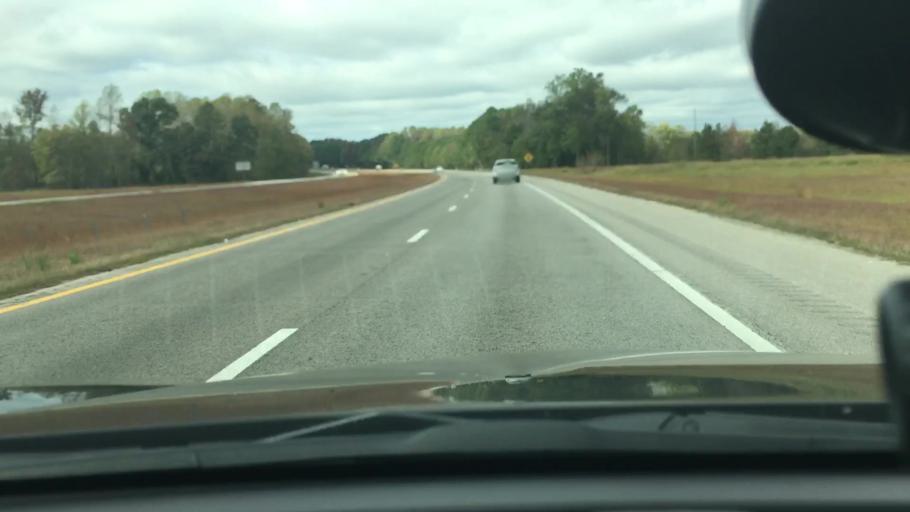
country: US
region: North Carolina
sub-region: Wilson County
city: Lucama
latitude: 35.7634
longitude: -78.0295
